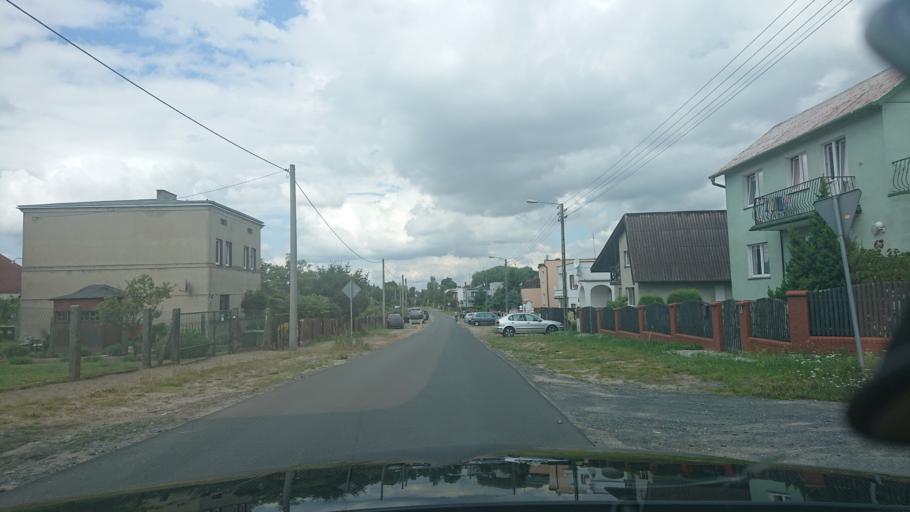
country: PL
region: Greater Poland Voivodeship
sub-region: Powiat gnieznienski
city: Gniezno
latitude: 52.5133
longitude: 17.6212
